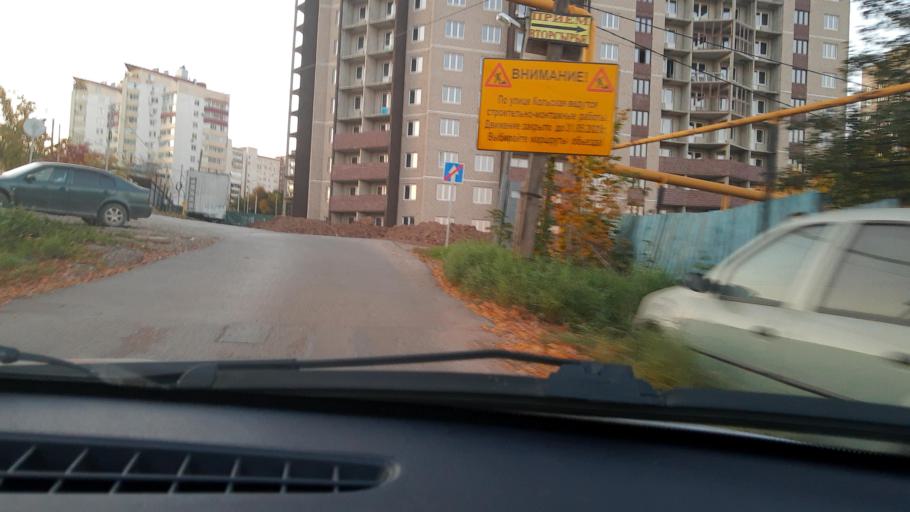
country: RU
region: Bashkortostan
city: Ufa
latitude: 54.7751
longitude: 56.0401
